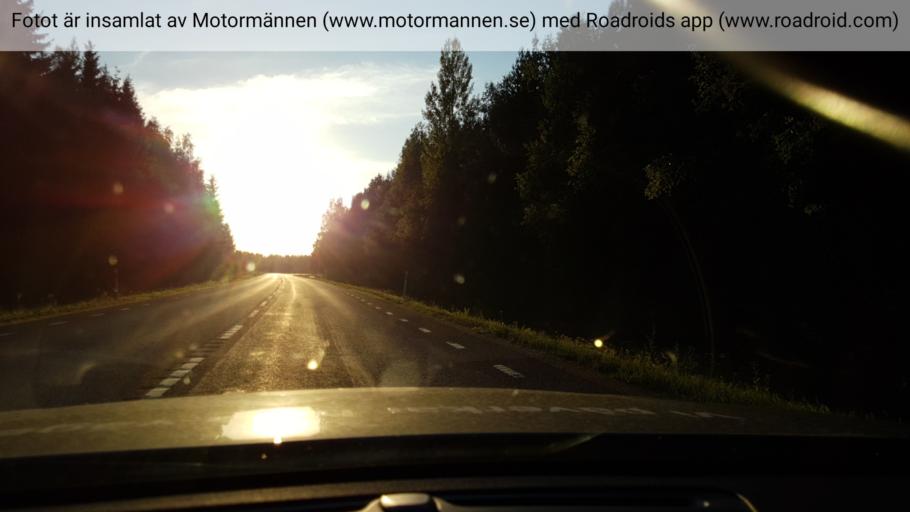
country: SE
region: OErebro
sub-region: Karlskoga Kommun
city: Karlskoga
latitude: 59.3831
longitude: 14.4852
